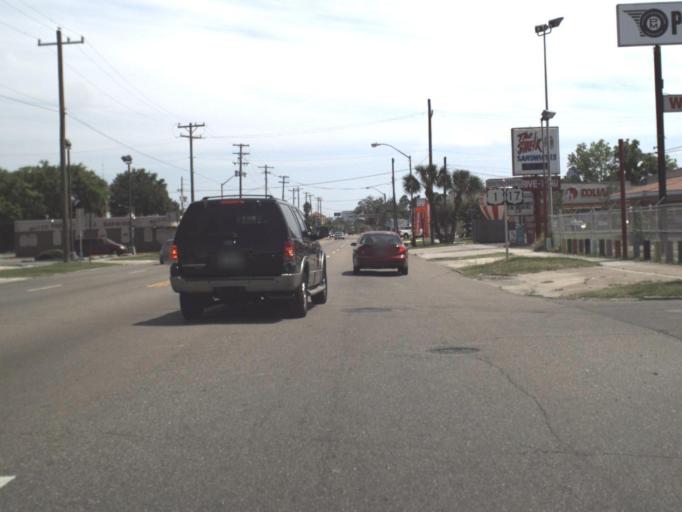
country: US
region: Florida
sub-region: Duval County
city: Jacksonville
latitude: 30.3551
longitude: -81.6539
